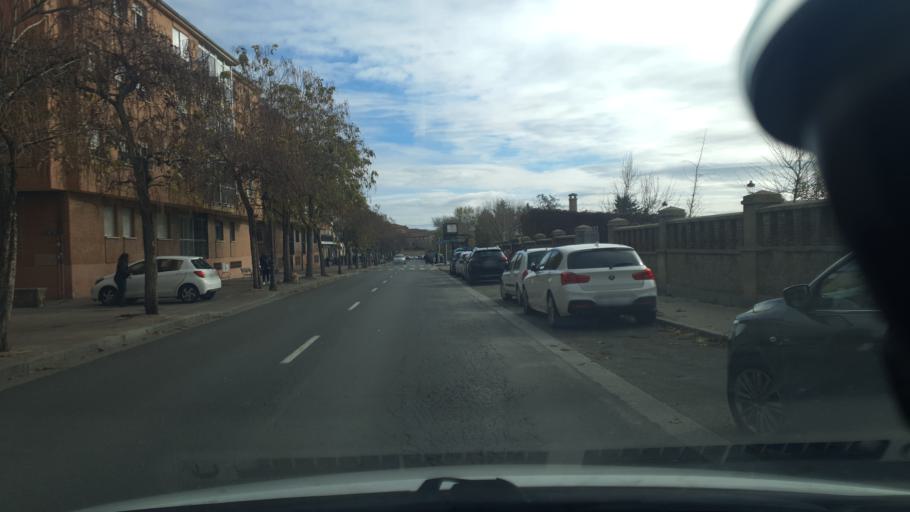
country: ES
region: Castille and Leon
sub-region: Provincia de Avila
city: Avila
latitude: 40.6514
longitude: -4.6928
